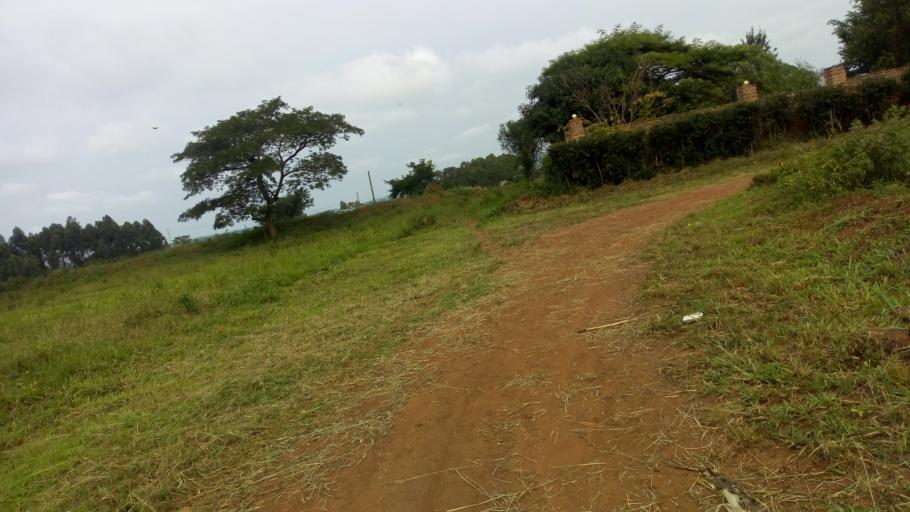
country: UG
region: Western Region
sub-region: Kiryandongo District
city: Kiryandongo
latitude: 1.8006
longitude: 32.0118
